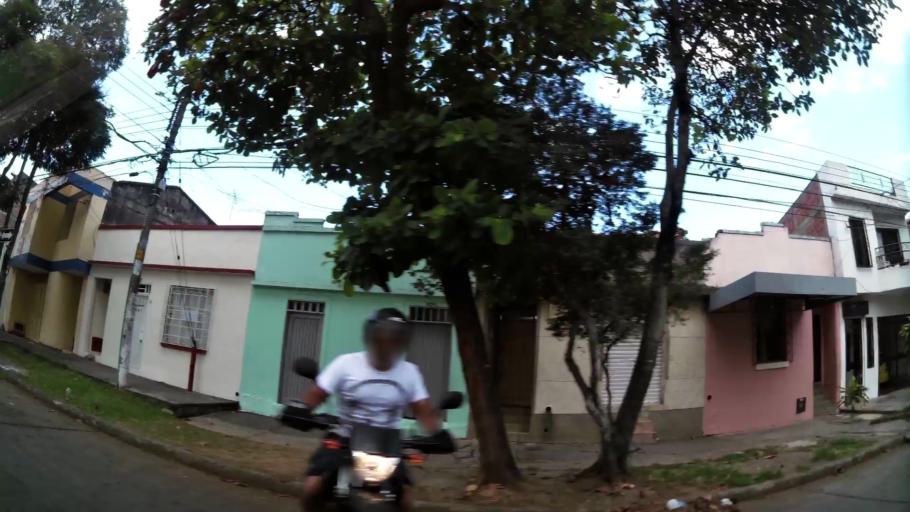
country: CO
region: Valle del Cauca
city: Cali
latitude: 3.4363
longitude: -76.5244
